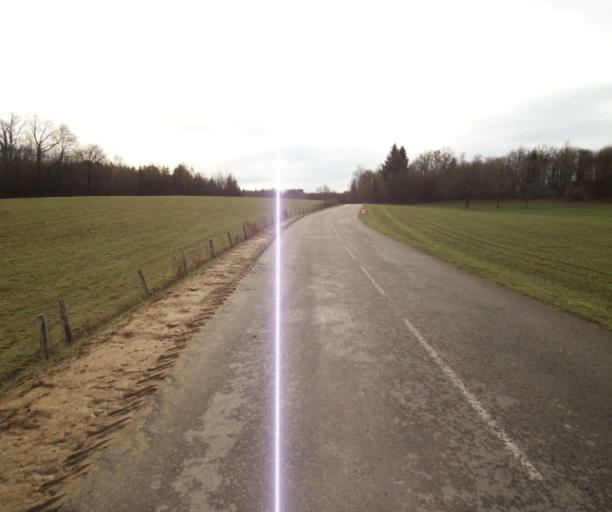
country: FR
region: Limousin
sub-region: Departement de la Correze
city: Chameyrat
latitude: 45.2521
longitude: 1.7011
